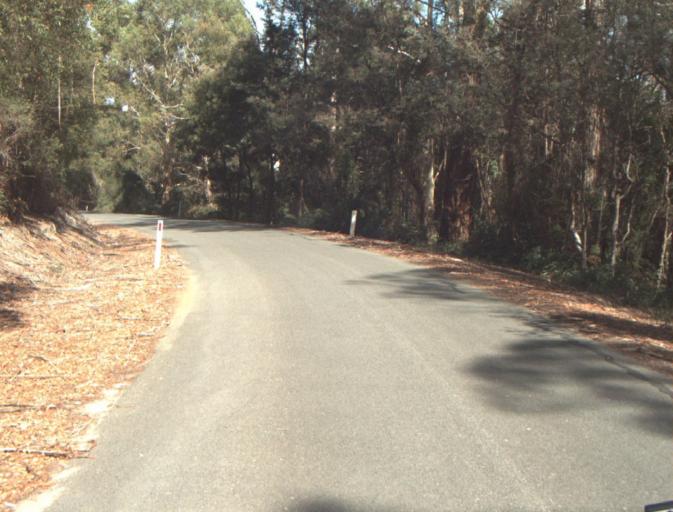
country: AU
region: Tasmania
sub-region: Launceston
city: Mayfield
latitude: -41.2576
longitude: 147.1834
